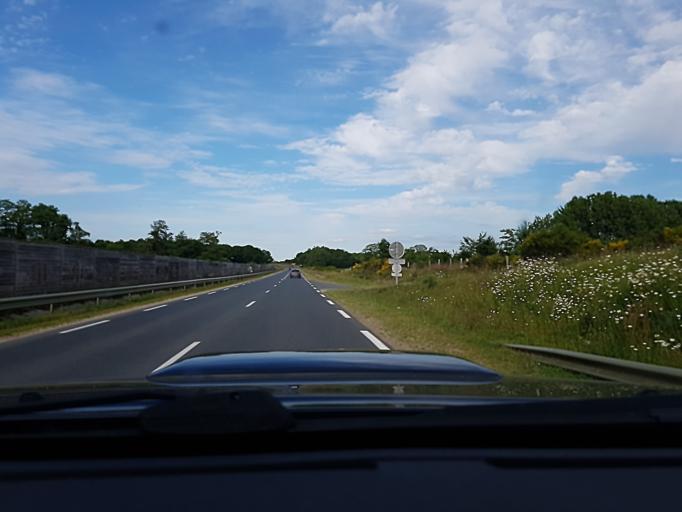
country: FR
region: Pays de la Loire
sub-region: Departement de la Vendee
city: Coex
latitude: 46.6896
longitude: -1.7558
